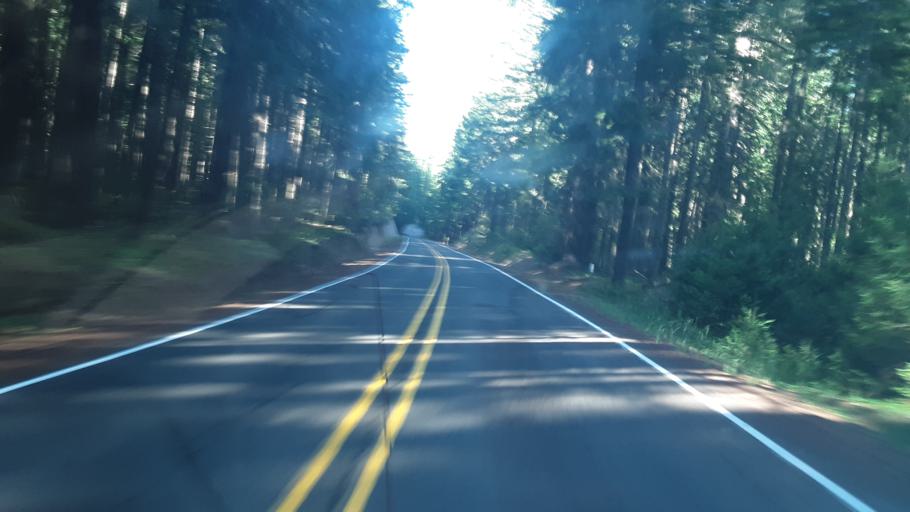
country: US
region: Oregon
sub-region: Jackson County
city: Shady Cove
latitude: 42.9407
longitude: -122.4188
